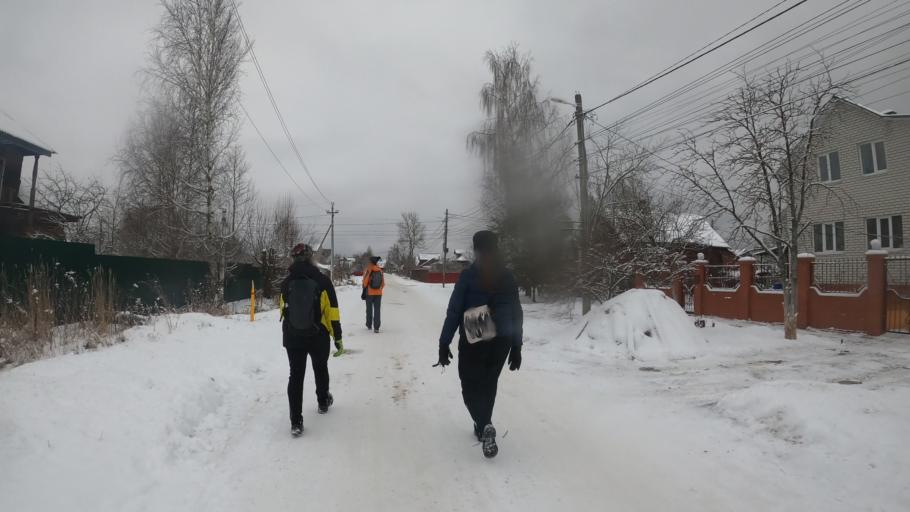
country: RU
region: Jaroslavl
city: Pereslavl'-Zalesskiy
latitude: 56.7330
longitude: 38.8349
